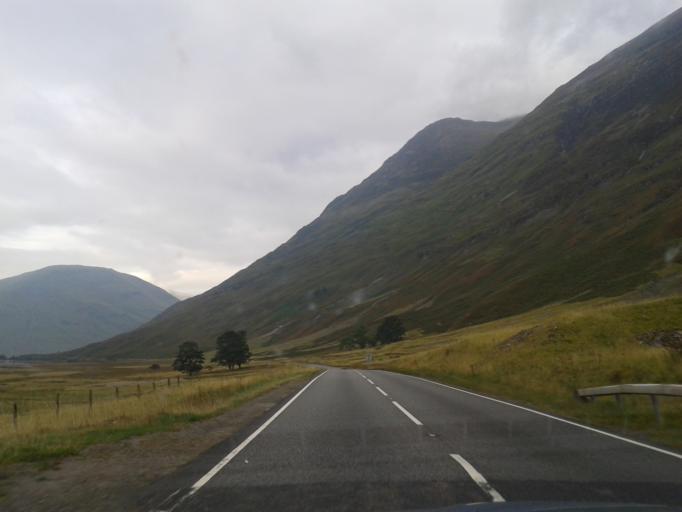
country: GB
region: Scotland
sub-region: Highland
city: Fort William
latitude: 56.6698
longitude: -5.0121
